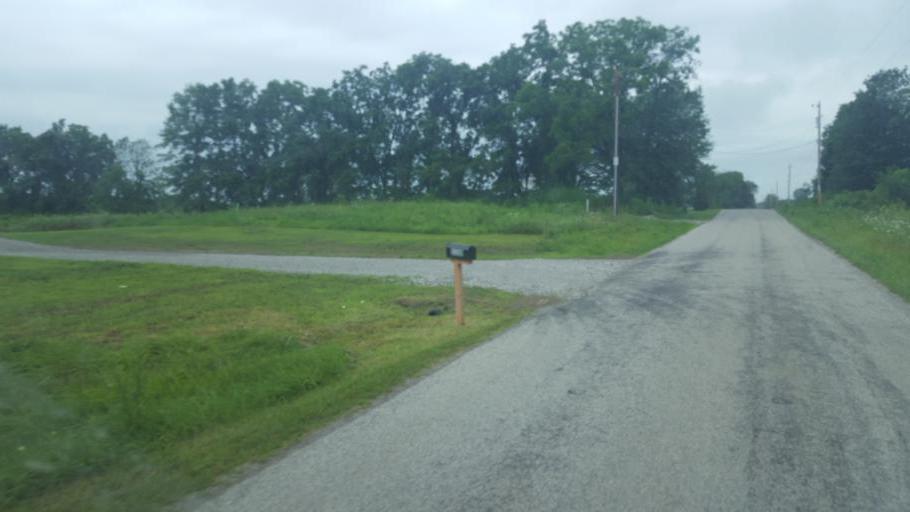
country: US
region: Ohio
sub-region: Knox County
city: Centerburg
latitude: 40.3811
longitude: -82.7710
